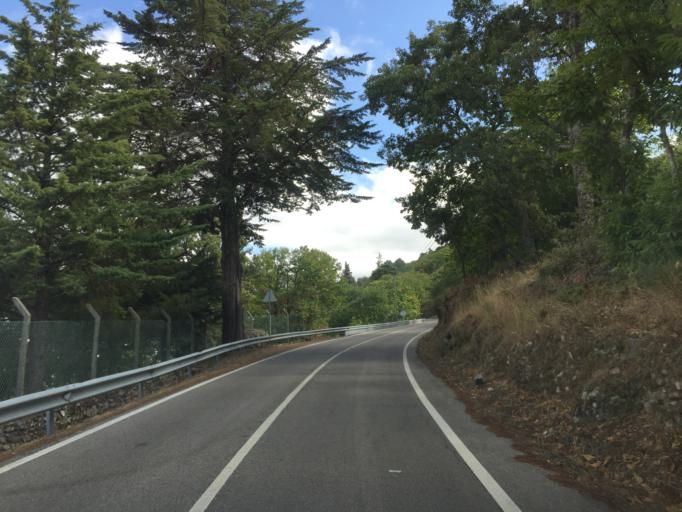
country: PT
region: Portalegre
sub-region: Marvao
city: Marvao
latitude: 39.4009
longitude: -7.3802
